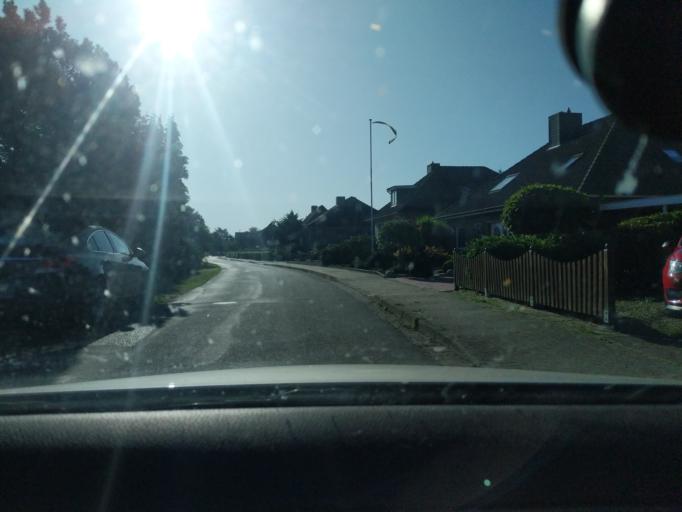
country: DE
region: Lower Saxony
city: Grunendeich
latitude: 53.5726
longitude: 9.6105
